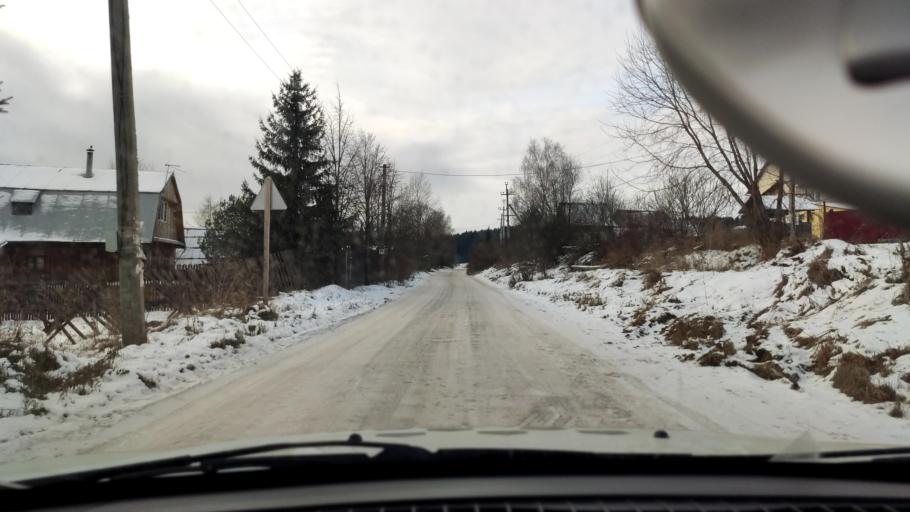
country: RU
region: Perm
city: Lobanovo
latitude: 57.8320
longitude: 56.3648
